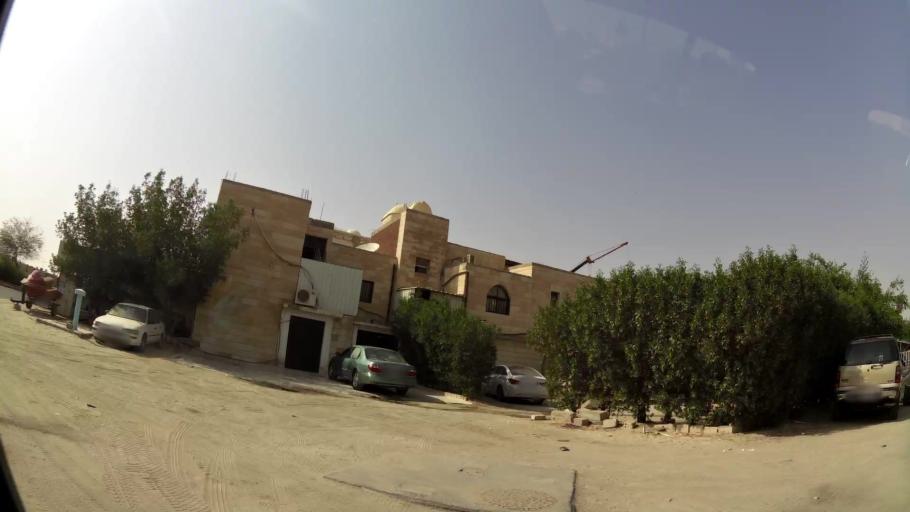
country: KW
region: Muhafazat al Jahra'
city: Al Jahra'
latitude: 29.3447
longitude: 47.6575
